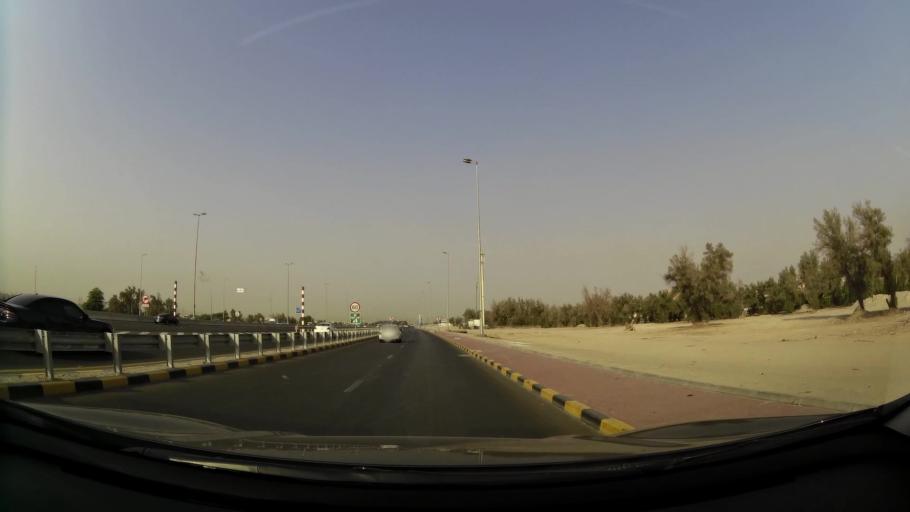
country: KW
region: Al Asimah
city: Ar Rabiyah
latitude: 29.3116
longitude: 47.8161
